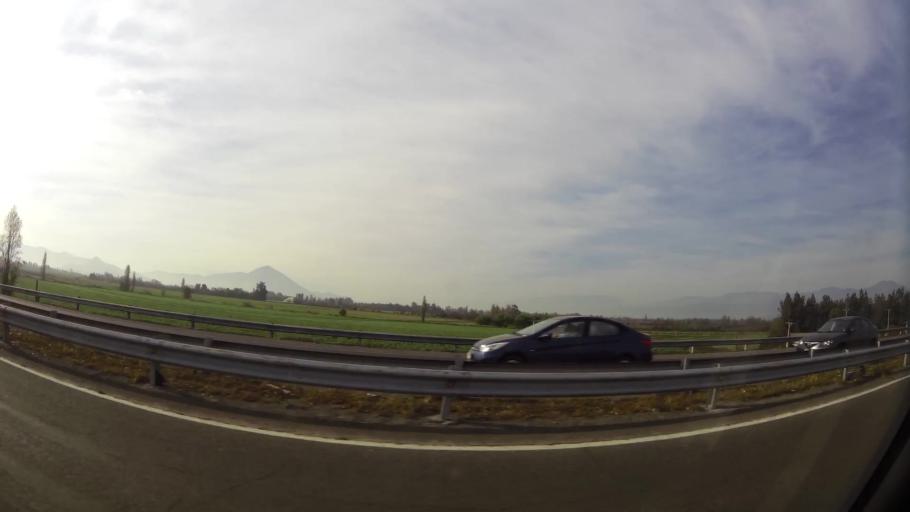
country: CL
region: Santiago Metropolitan
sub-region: Provincia de Talagante
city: Talagante
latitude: -33.6666
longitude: -70.9106
